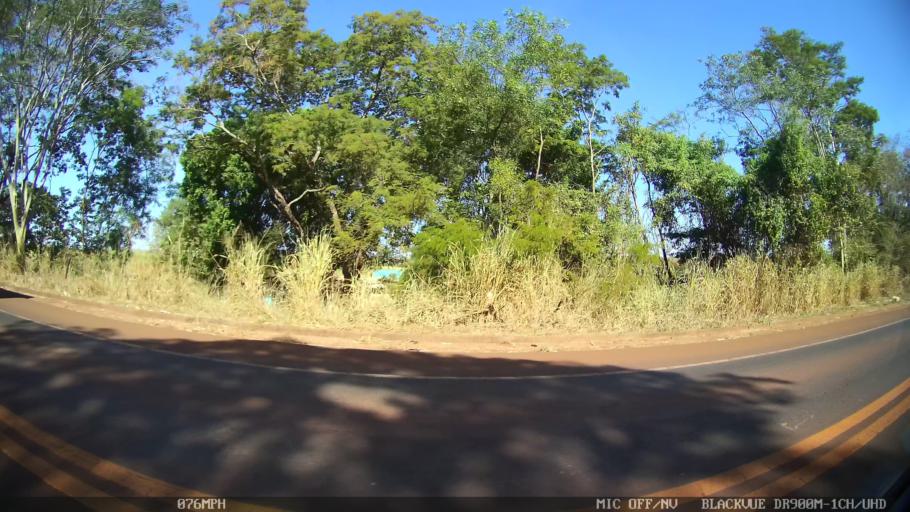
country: BR
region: Sao Paulo
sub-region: Sao Joaquim Da Barra
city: Sao Joaquim da Barra
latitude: -20.5390
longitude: -47.8202
